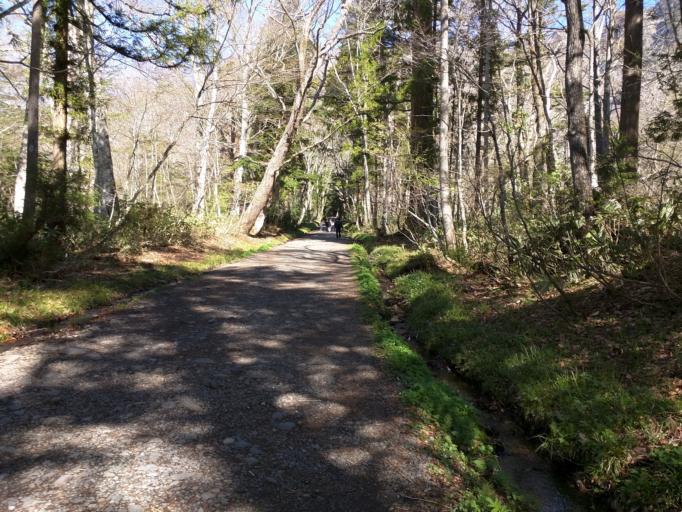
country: JP
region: Nagano
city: Nagano-shi
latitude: 36.7595
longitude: 138.0725
